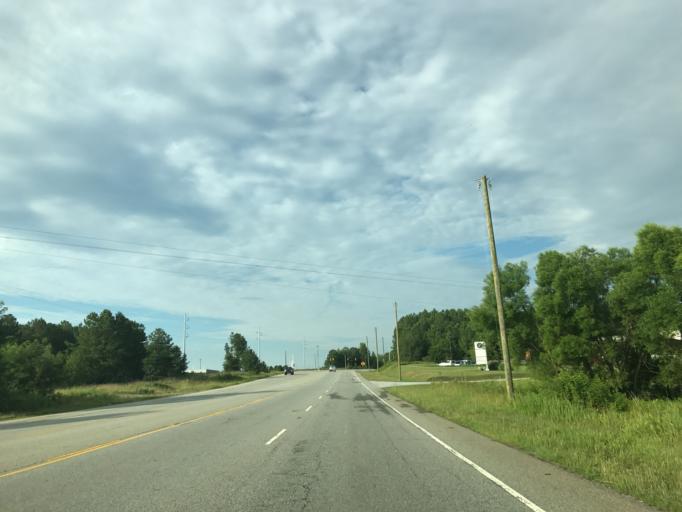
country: US
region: South Carolina
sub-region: Greenville County
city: Greer
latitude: 34.9020
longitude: -82.1928
